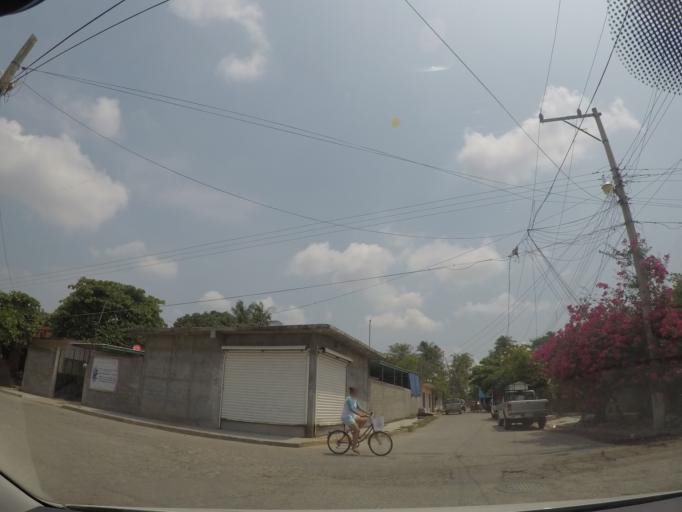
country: MX
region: Oaxaca
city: El Espinal
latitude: 16.4919
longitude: -95.0427
